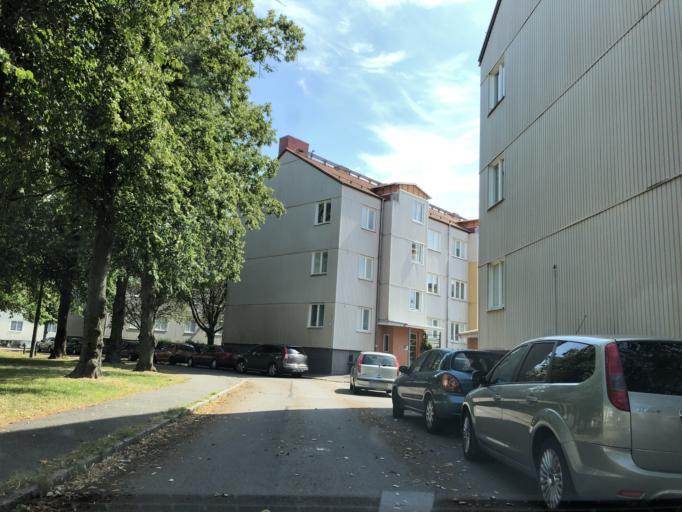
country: SE
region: Vaestra Goetaland
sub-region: Goteborg
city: Majorna
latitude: 57.7164
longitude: 11.9259
